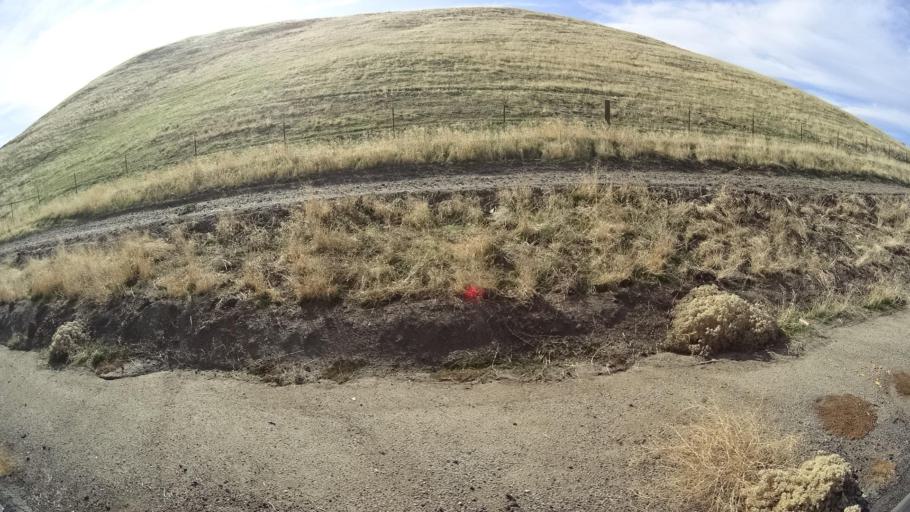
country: US
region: California
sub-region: Kern County
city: Oildale
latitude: 35.6103
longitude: -118.9277
